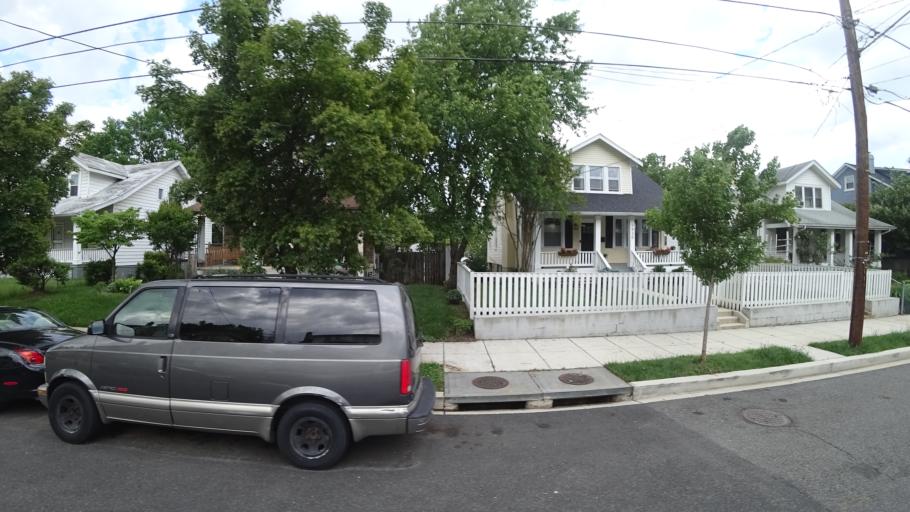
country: US
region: Maryland
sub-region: Prince George's County
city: Mount Rainier
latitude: 38.9311
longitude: -76.9777
